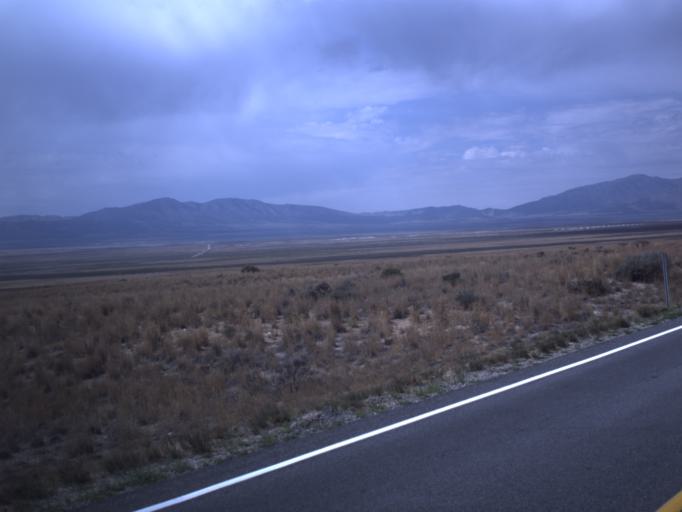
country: US
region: Utah
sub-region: Utah County
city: Eagle Mountain
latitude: 40.2630
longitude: -112.2344
